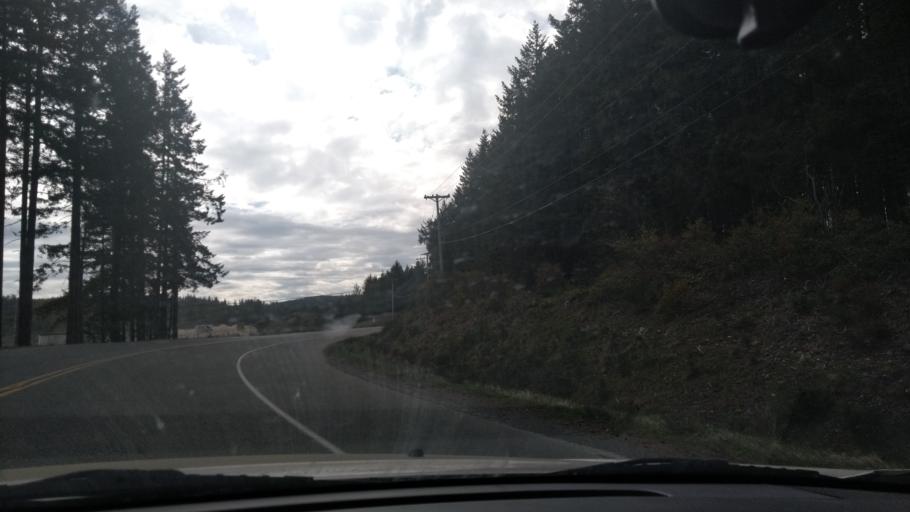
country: CA
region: British Columbia
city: Campbell River
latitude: 50.0078
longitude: -125.3564
